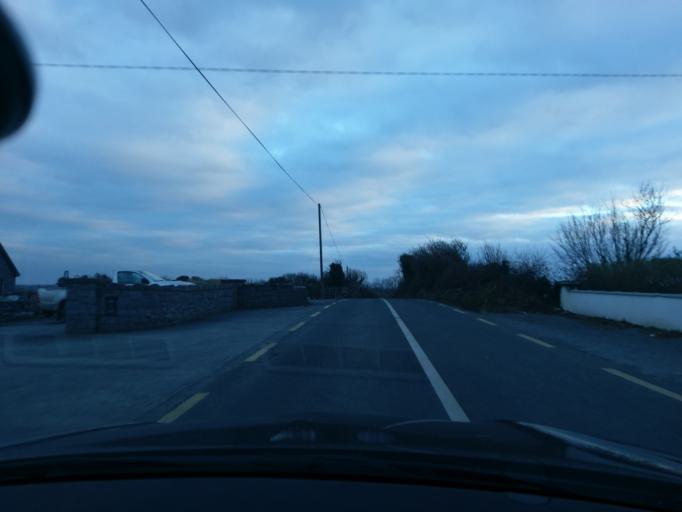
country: IE
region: Connaught
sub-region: County Galway
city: Athenry
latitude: 53.3671
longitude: -8.7741
